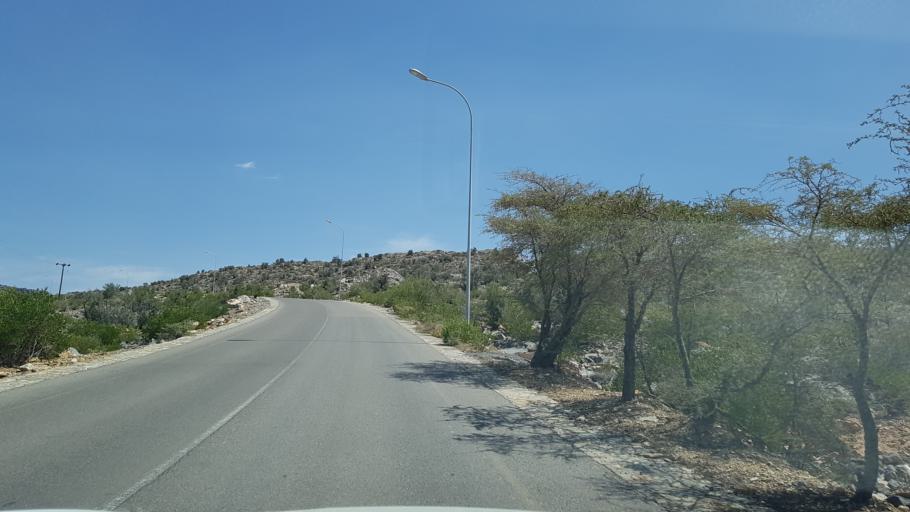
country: OM
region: Al Batinah
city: Bayt al `Awabi
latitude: 23.1399
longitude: 57.5408
